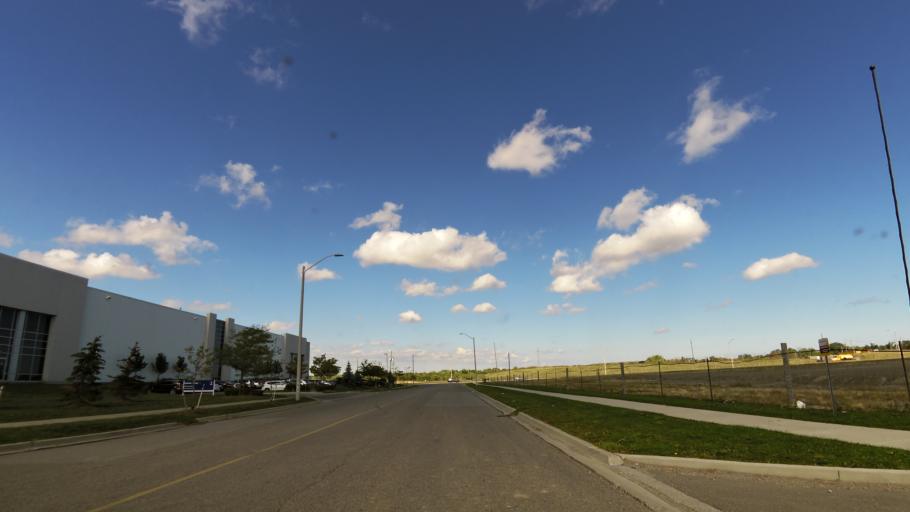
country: CA
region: Ontario
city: Mississauga
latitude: 43.5852
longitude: -79.7309
